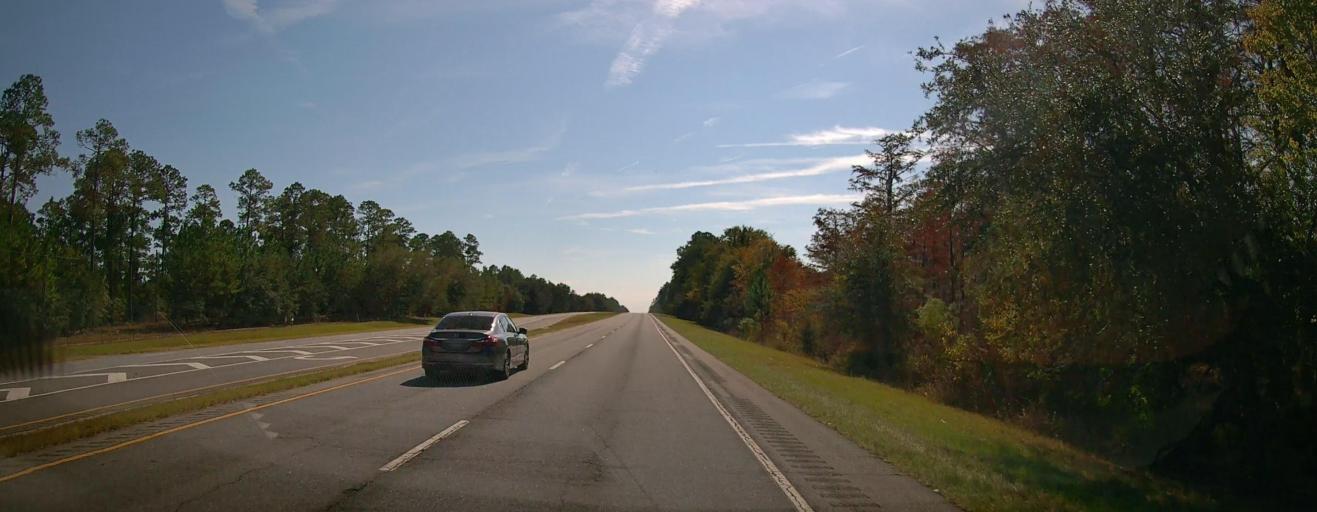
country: US
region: Georgia
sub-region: Lee County
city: Leesburg
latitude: 31.6985
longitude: -83.9918
